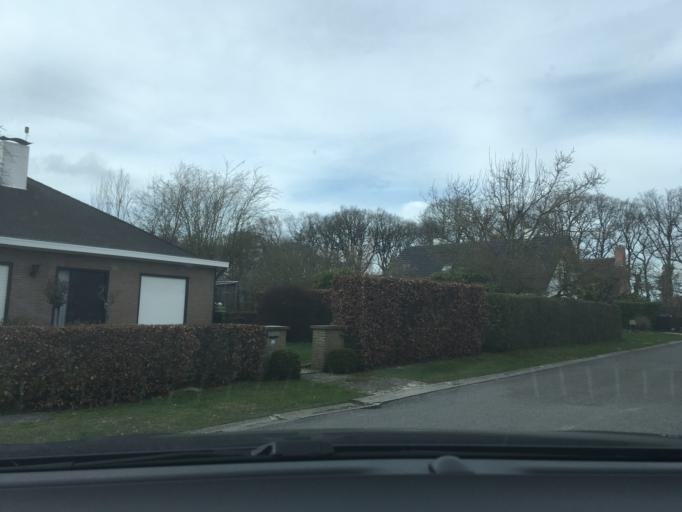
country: BE
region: Flanders
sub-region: Provincie West-Vlaanderen
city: Pittem
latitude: 50.9622
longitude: 3.2407
